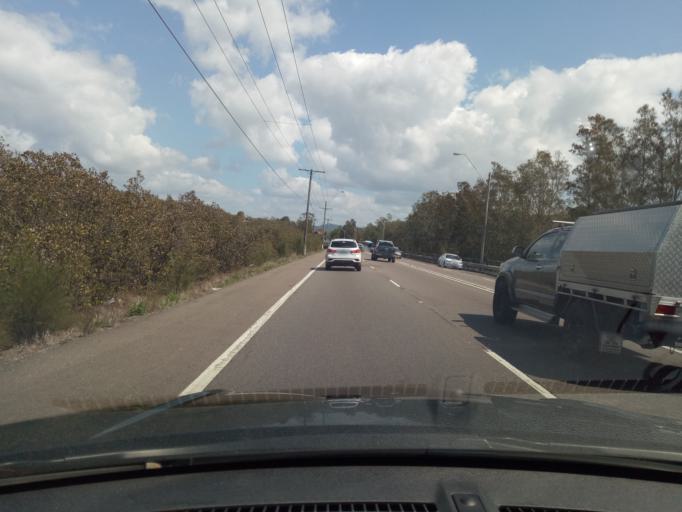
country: AU
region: New South Wales
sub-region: Gosford Shire
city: East Gosford
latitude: -33.4372
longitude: 151.3637
